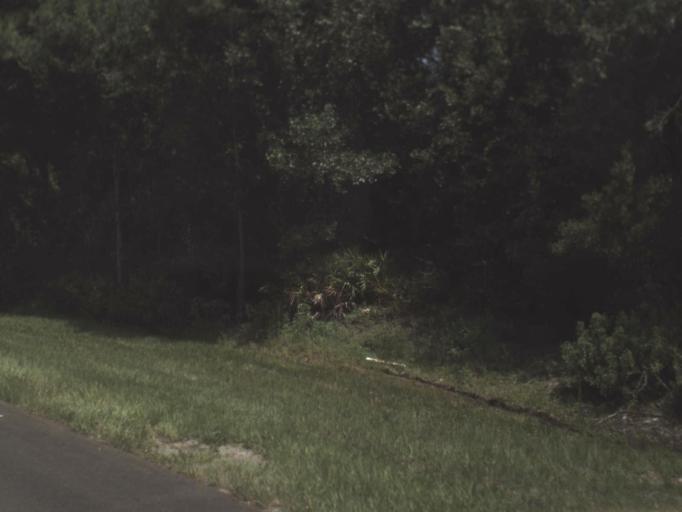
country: US
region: Florida
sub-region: Alachua County
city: Alachua
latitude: 29.7591
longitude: -82.3585
